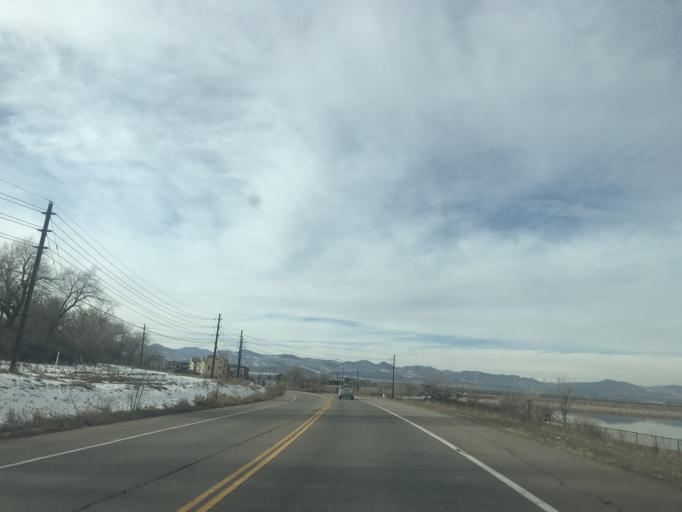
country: US
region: Colorado
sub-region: Arapahoe County
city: Columbine Valley
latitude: 39.5660
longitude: -105.0154
